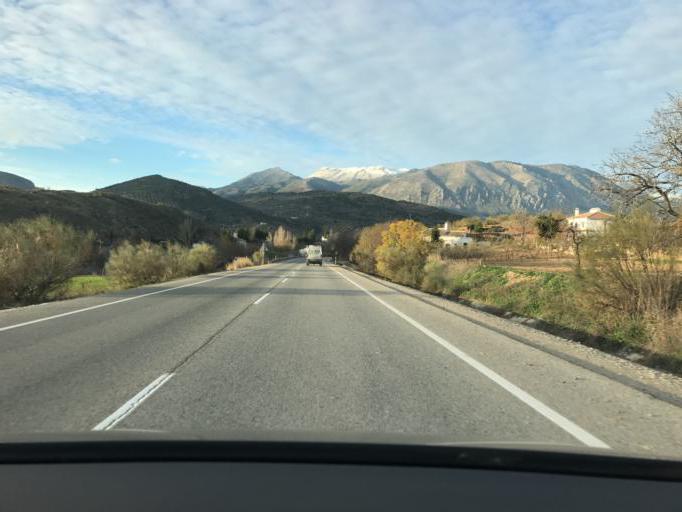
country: ES
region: Andalusia
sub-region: Provincia de Jaen
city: Huelma
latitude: 37.6443
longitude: -3.4177
